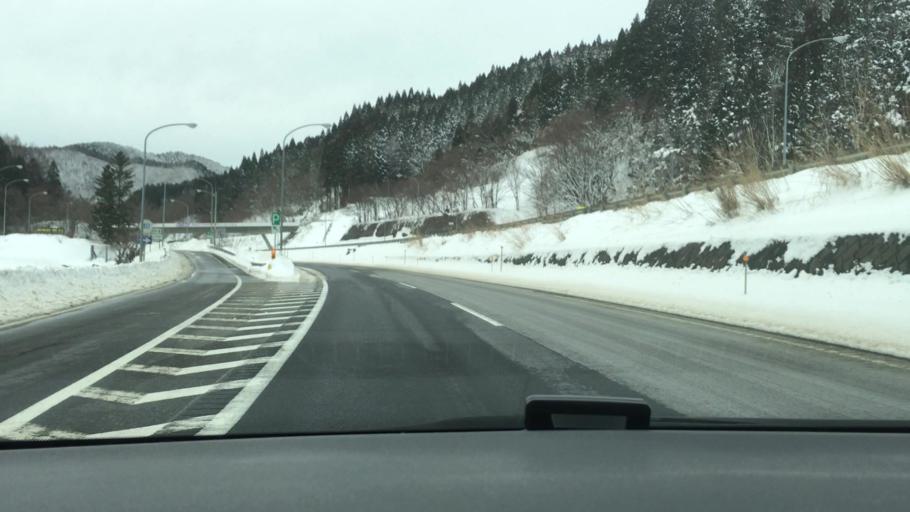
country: JP
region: Akita
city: Hanawa
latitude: 40.1258
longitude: 140.8369
